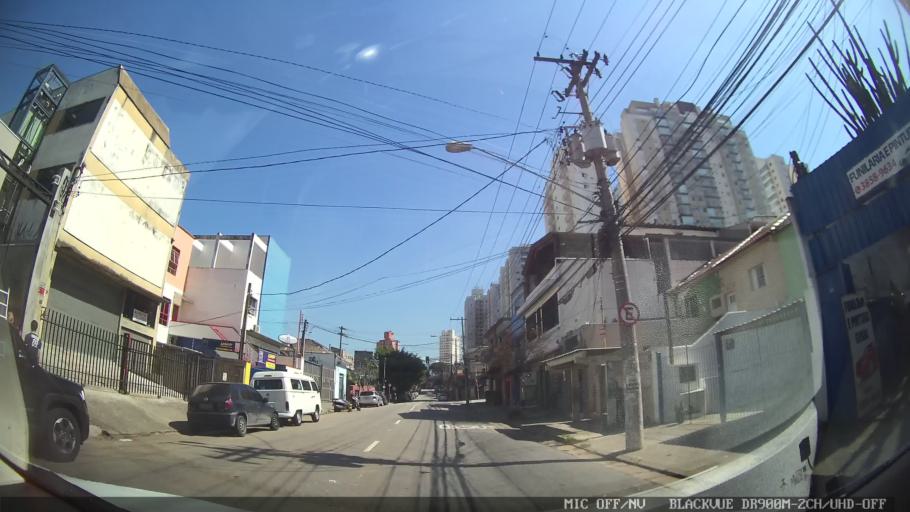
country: BR
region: Sao Paulo
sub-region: Sao Paulo
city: Sao Paulo
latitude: -23.5118
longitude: -46.6547
